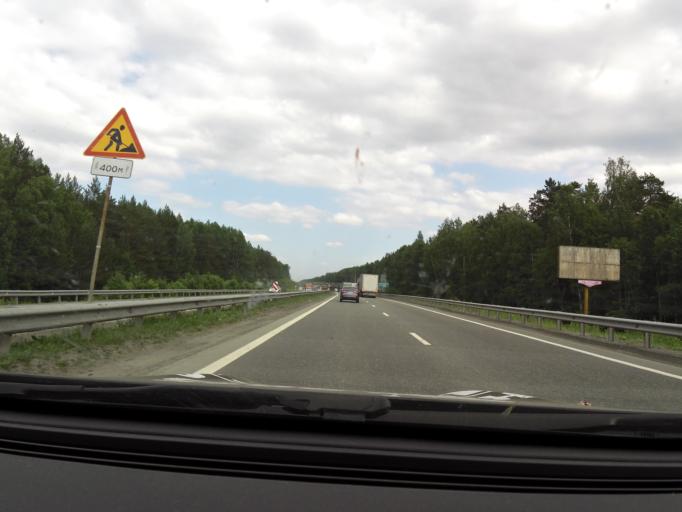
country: RU
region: Sverdlovsk
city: Talitsa
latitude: 56.8397
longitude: 60.1100
